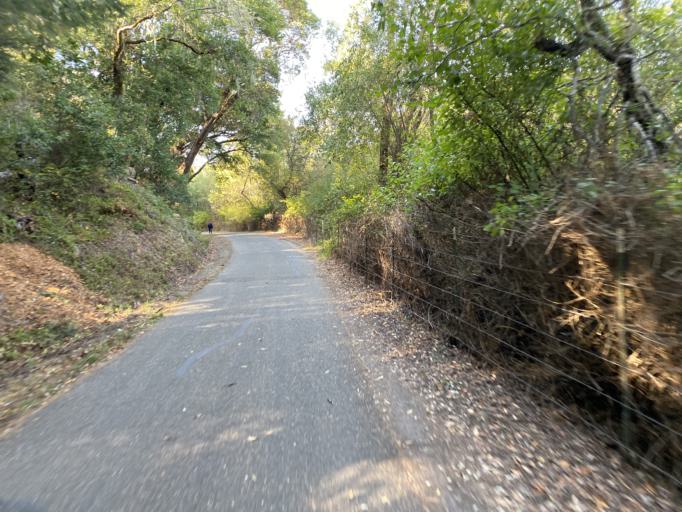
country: US
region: California
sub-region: San Mateo County
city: Hillsborough
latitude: 37.5661
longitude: -122.4006
